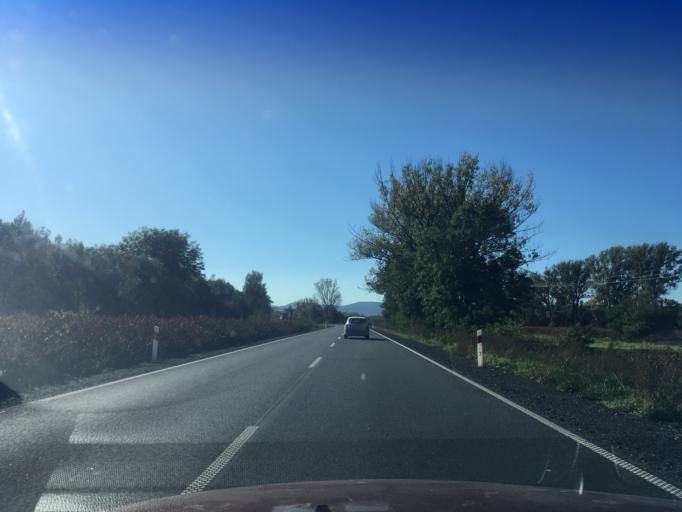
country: DE
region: Saxony
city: Zittau
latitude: 50.9058
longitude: 14.8487
